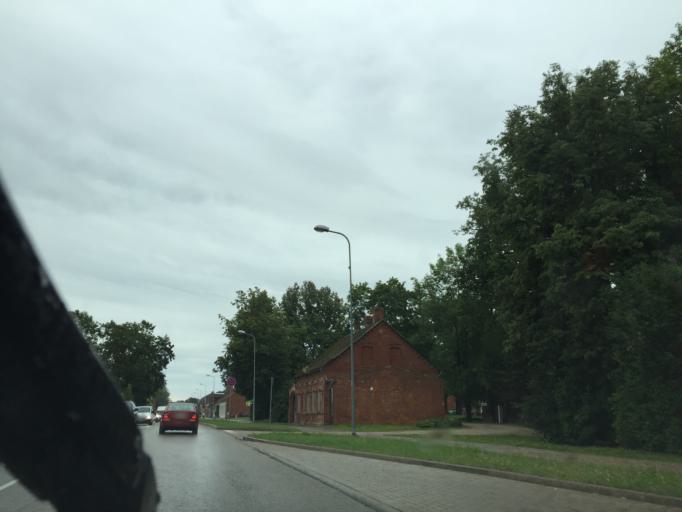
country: LV
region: Jekabpils Rajons
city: Jekabpils
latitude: 56.5060
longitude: 25.8639
